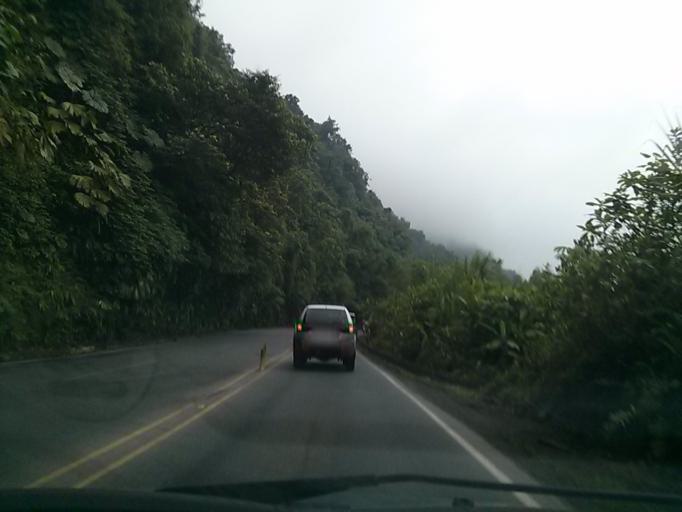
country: CR
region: San Jose
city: Dulce Nombre de Jesus
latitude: 10.0901
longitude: -83.9824
